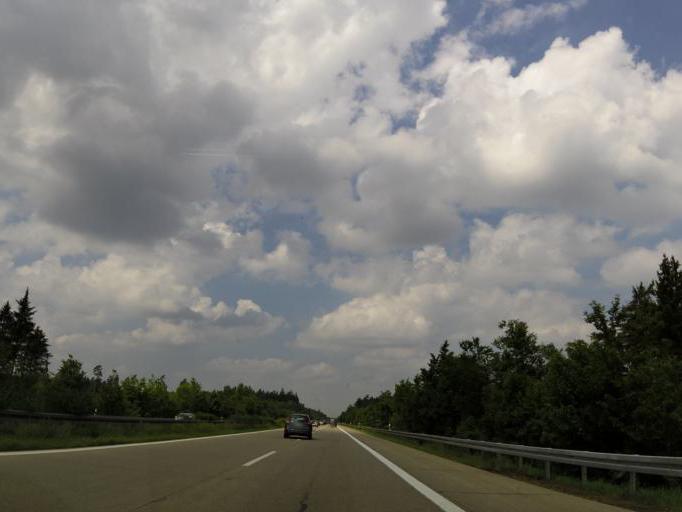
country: DE
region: Baden-Wuerttemberg
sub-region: Regierungsbezirk Stuttgart
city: Ellenberg
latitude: 49.0308
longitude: 10.1918
